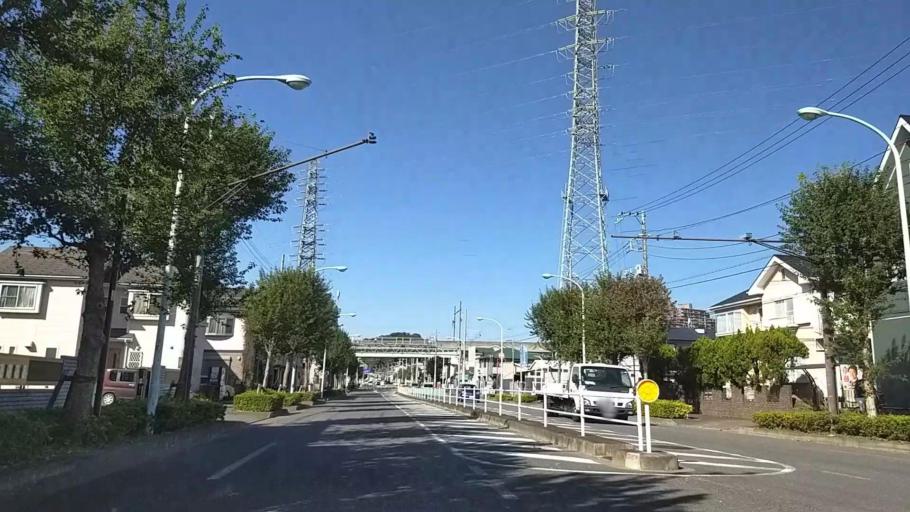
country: JP
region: Tokyo
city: Hachioji
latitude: 35.5980
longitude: 139.3660
